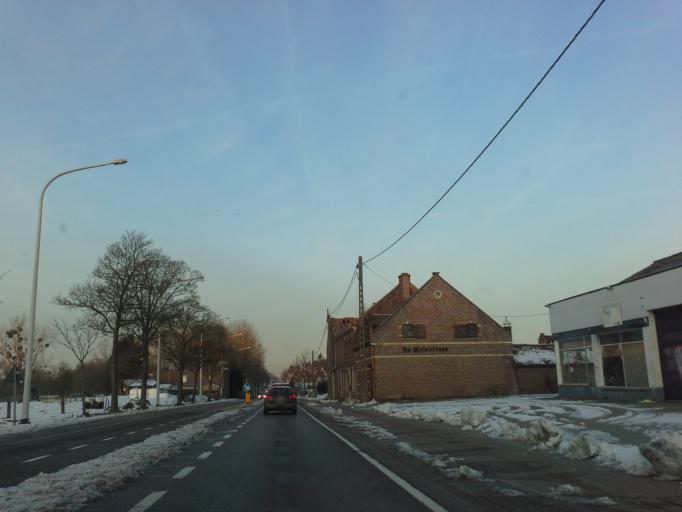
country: BE
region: Flanders
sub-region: Provincie Vlaams-Brabant
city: Bierbeek
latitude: 50.8600
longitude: 4.7733
